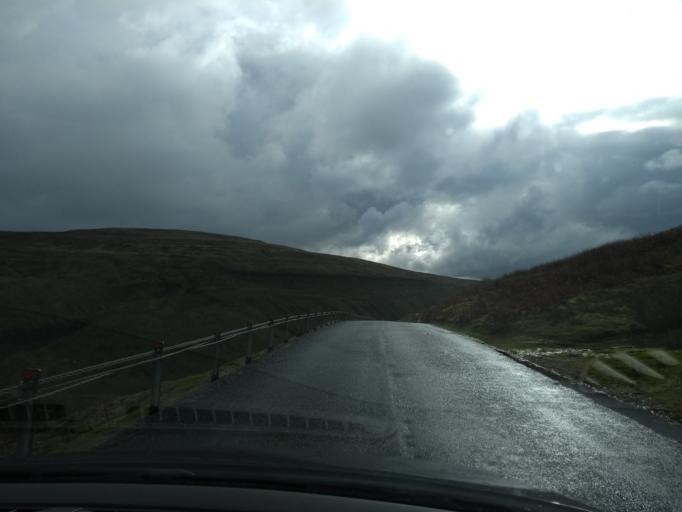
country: GB
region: England
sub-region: Cumbria
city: Kirkby Stephen
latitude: 54.3662
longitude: -2.1891
